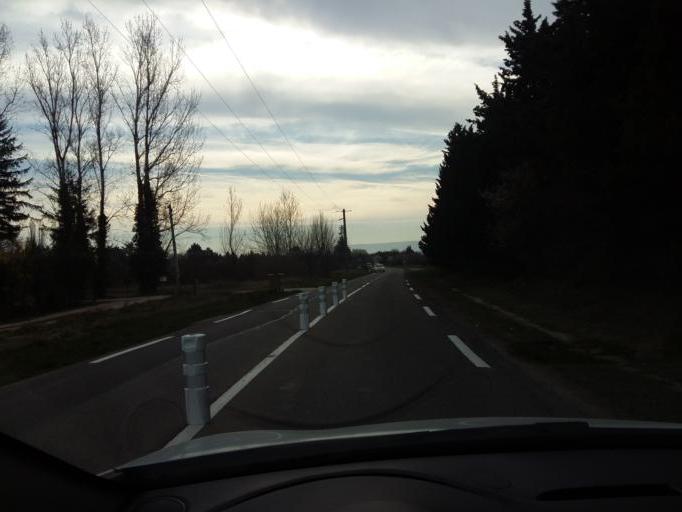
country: FR
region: Provence-Alpes-Cote d'Azur
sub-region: Departement du Vaucluse
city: L'Isle-sur-la-Sorgue
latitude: 43.9242
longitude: 5.0694
